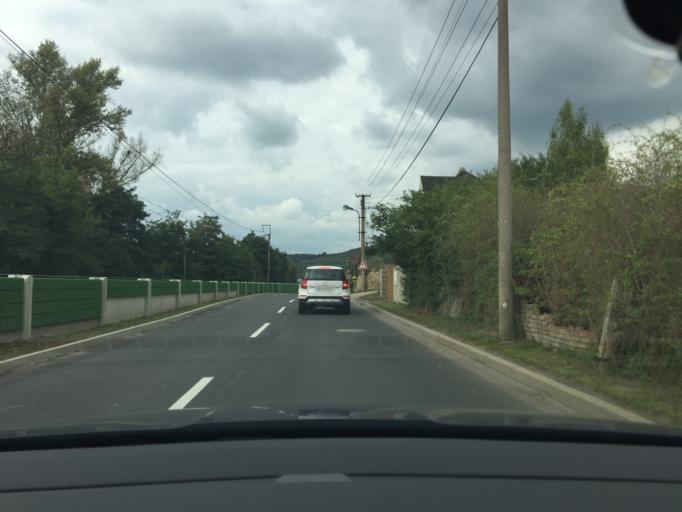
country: CZ
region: Ustecky
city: Lovosice
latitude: 50.5328
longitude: 14.0687
